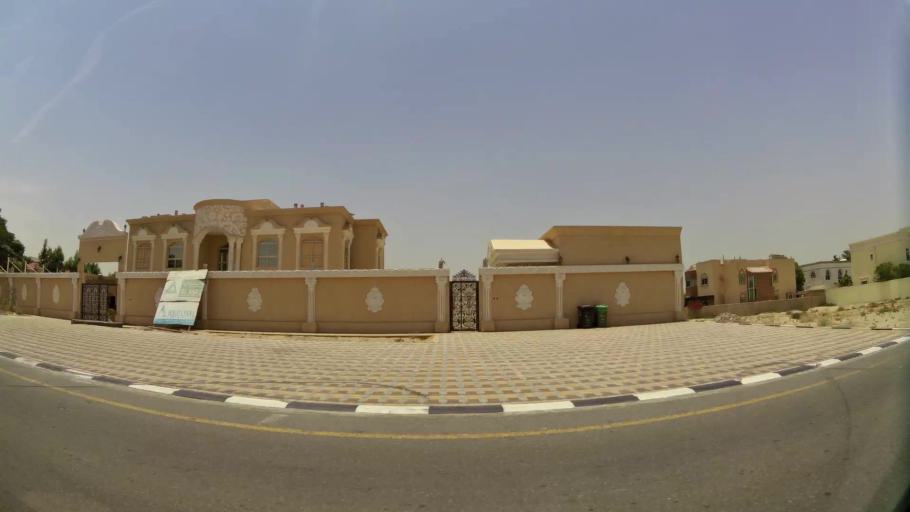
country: AE
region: Ash Shariqah
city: Sharjah
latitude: 25.2463
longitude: 55.4594
